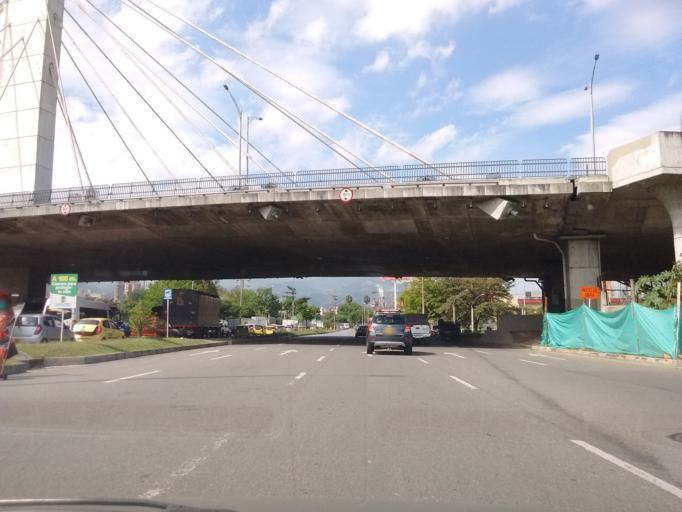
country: CO
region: Antioquia
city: Itagui
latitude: 6.2047
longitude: -75.5799
